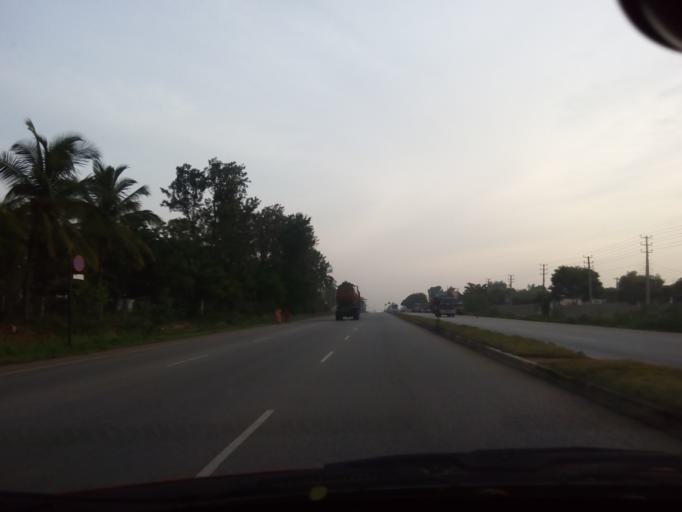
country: IN
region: Karnataka
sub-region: Bangalore Rural
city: Devanhalli
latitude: 13.2803
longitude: 77.7223
